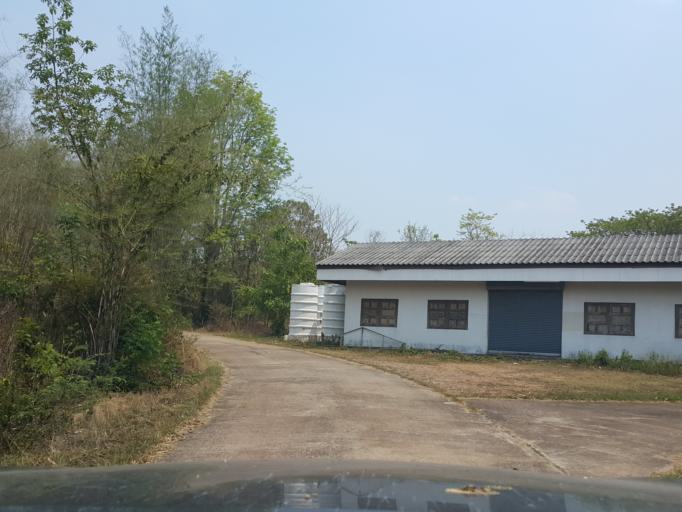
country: TH
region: Lampang
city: Mae Phrik
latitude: 17.5683
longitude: 99.0861
